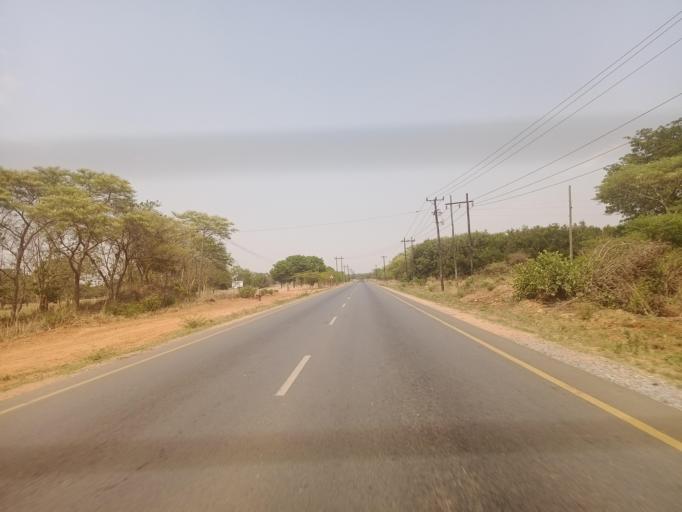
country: ZM
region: Lusaka
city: Lusaka
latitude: -15.2792
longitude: 28.3974
